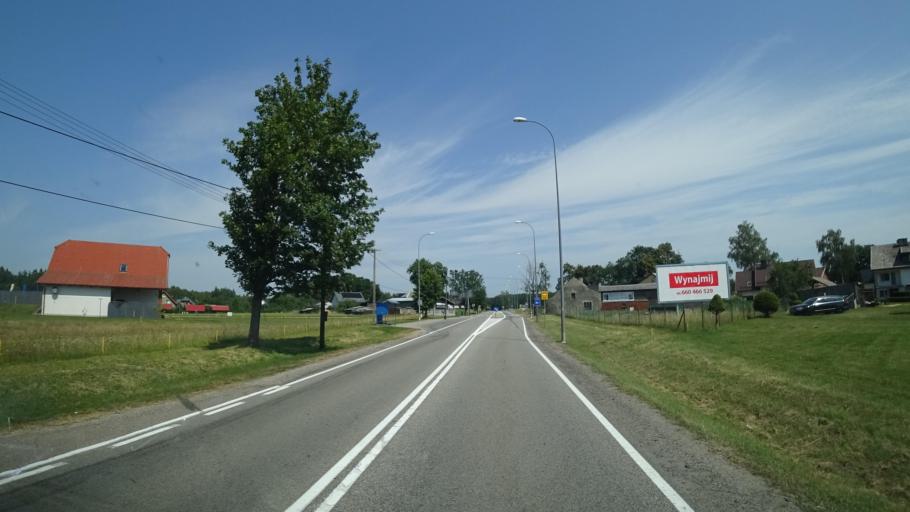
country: PL
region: Pomeranian Voivodeship
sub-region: Powiat koscierski
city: Grabowo Koscierskie
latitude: 54.1849
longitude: 18.0985
